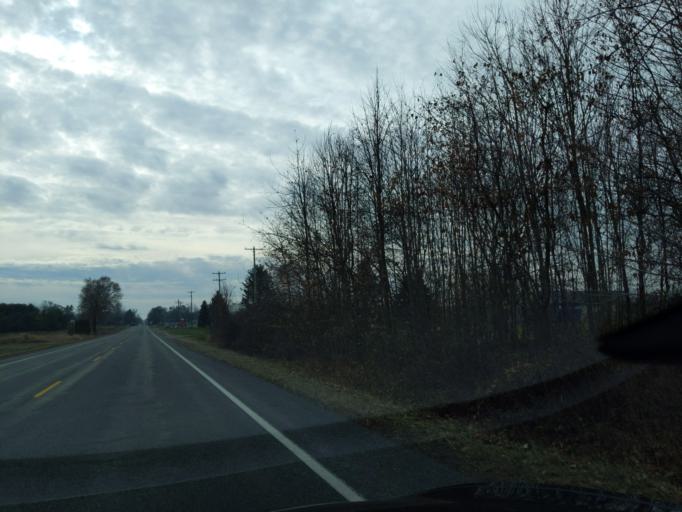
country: US
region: Michigan
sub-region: Ingham County
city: Holt
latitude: 42.5869
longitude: -84.5230
